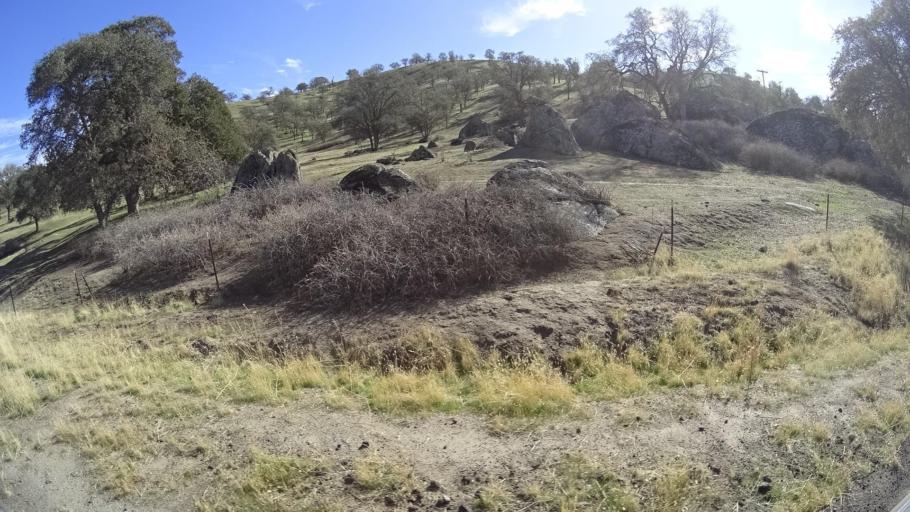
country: US
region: California
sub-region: Kern County
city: Oildale
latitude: 35.6344
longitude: -118.8397
